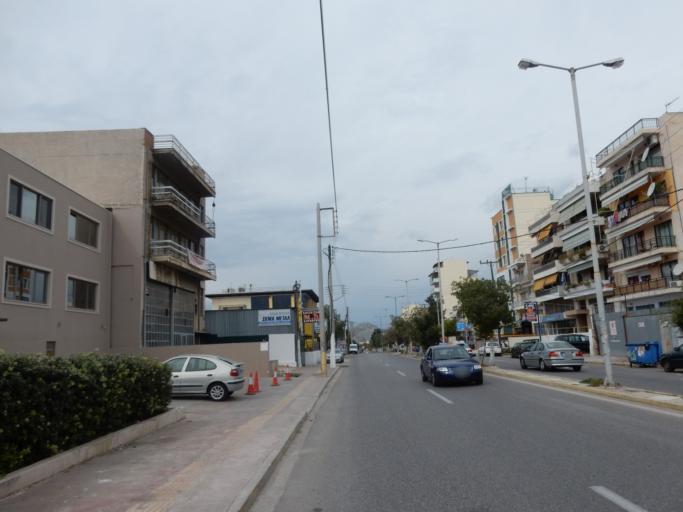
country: GR
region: Attica
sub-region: Nomos Piraios
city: Perama
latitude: 37.9635
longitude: 23.5645
